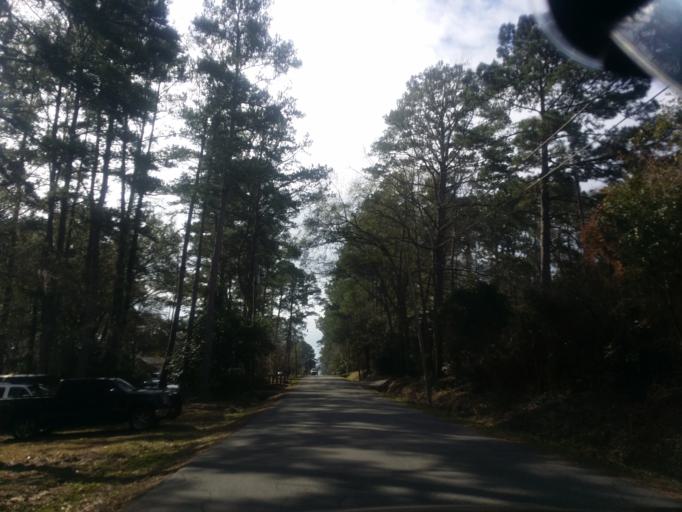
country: US
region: Florida
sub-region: Leon County
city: Tallahassee
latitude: 30.4543
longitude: -84.2401
